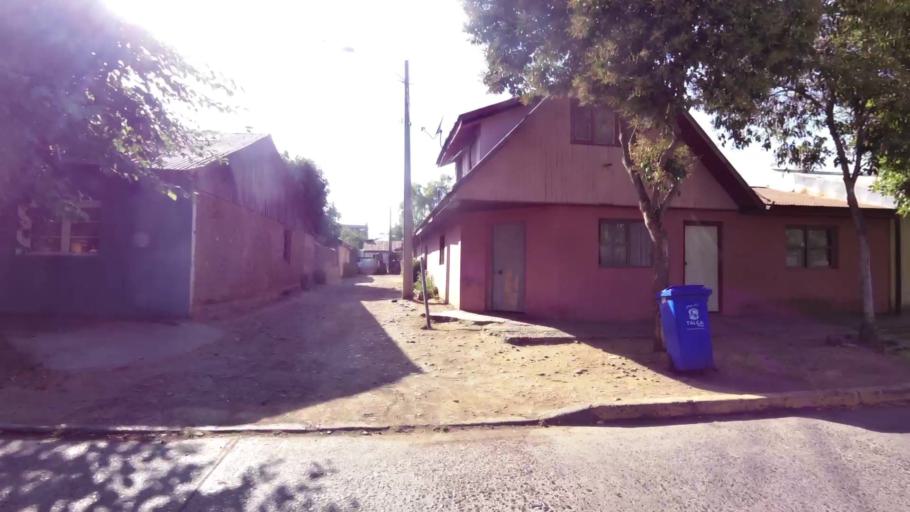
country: CL
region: Maule
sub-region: Provincia de Talca
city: Talca
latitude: -35.4096
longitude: -71.6626
